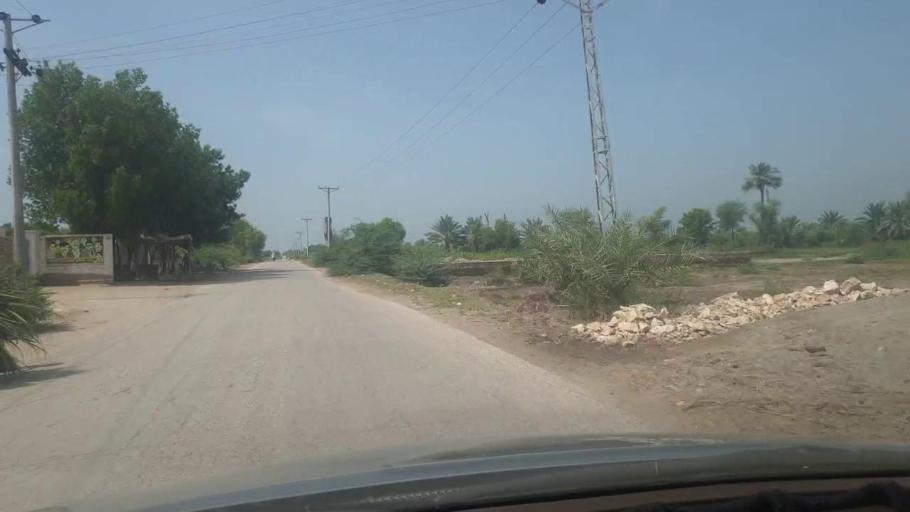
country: PK
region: Sindh
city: Ranipur
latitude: 27.2953
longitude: 68.6084
